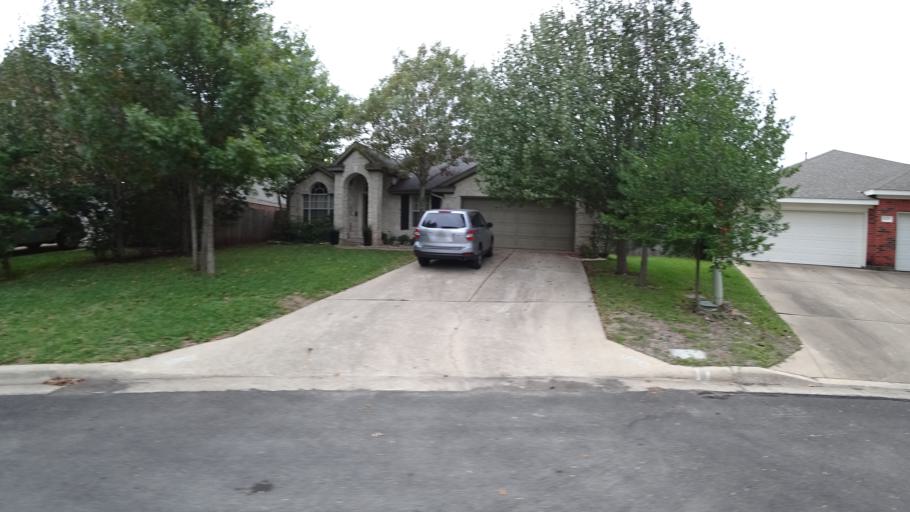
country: US
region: Texas
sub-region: Travis County
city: Shady Hollow
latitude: 30.1861
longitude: -97.8846
